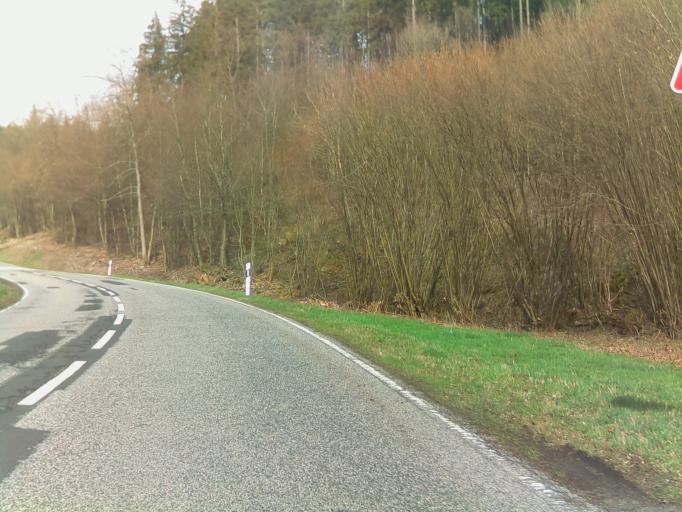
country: DE
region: Rheinland-Pfalz
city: Munchwald
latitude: 49.9105
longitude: 7.6695
